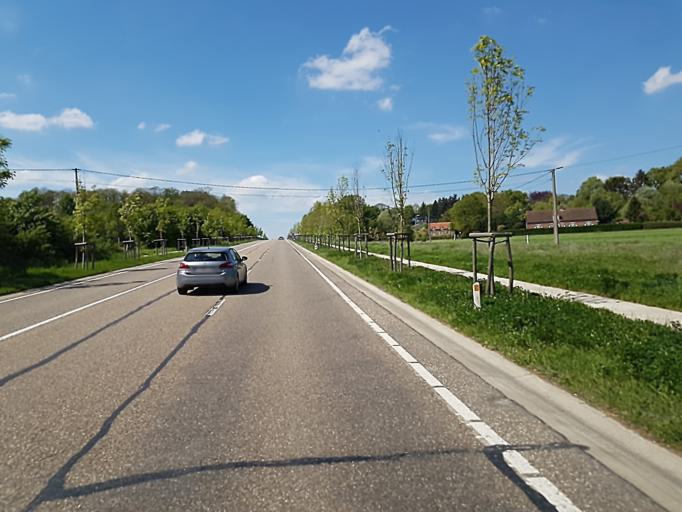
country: BE
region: Flanders
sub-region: Provincie Vlaams-Brabant
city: Lubbeek
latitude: 50.9144
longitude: 4.8609
